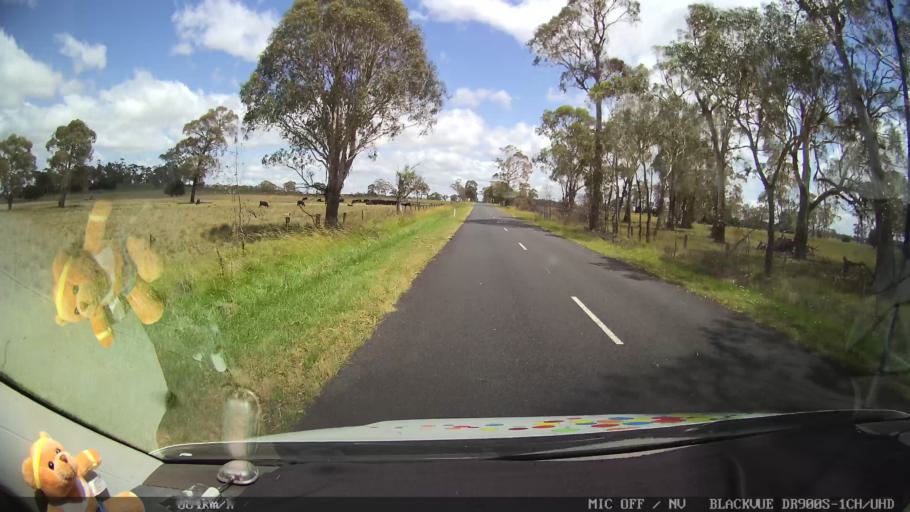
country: AU
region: New South Wales
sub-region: Glen Innes Severn
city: Glen Innes
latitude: -29.6262
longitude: 151.6714
